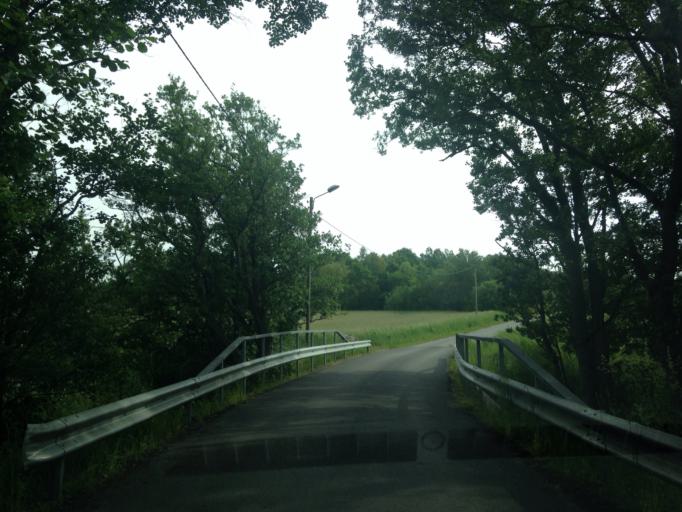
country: SE
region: Vaestra Goetaland
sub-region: Goteborg
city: Majorna
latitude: 57.7535
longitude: 11.8677
